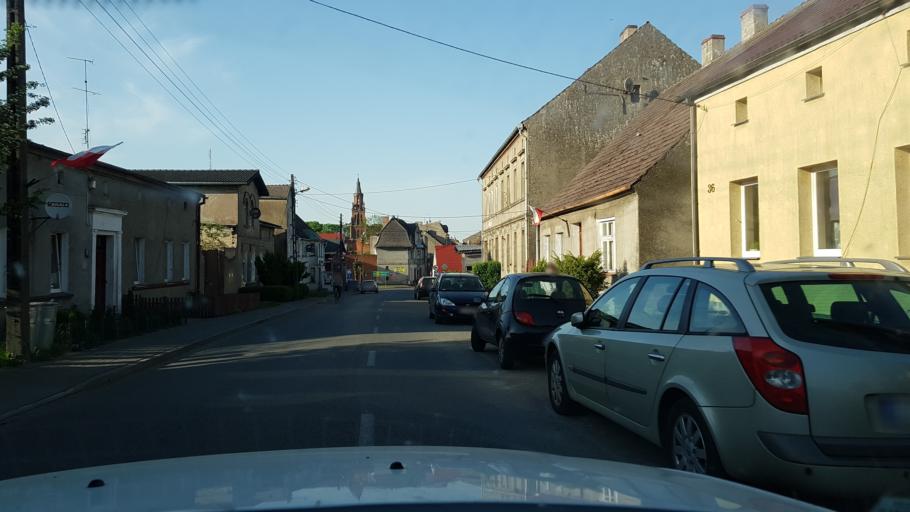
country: PL
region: West Pomeranian Voivodeship
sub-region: Powiat lobeski
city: Dobra
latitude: 53.5836
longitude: 15.3072
